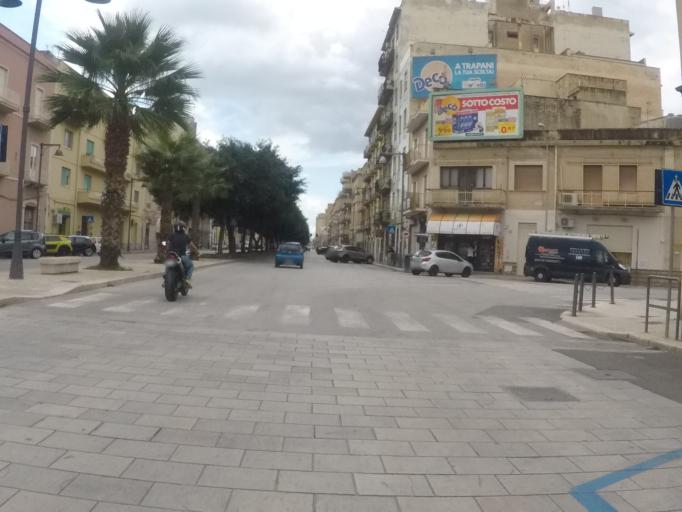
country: IT
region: Sicily
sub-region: Trapani
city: Trapani
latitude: 38.0206
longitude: 12.5329
